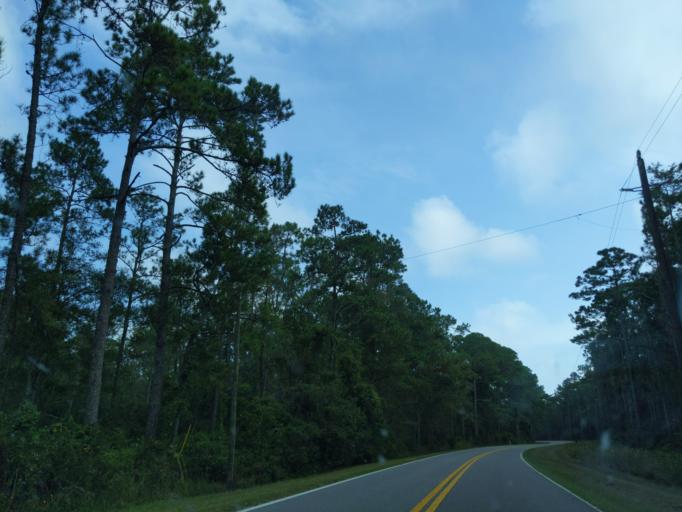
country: US
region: Florida
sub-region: Wakulla County
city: Crawfordville
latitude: 30.1021
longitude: -84.3049
